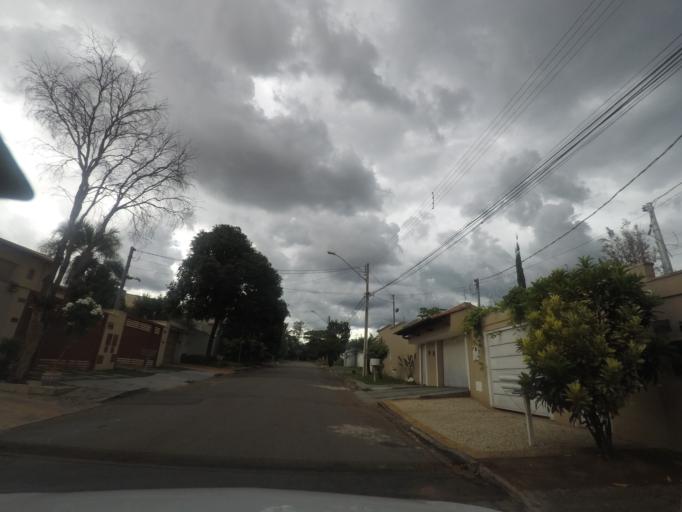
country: BR
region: Goias
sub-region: Goiania
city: Goiania
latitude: -16.6422
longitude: -49.2250
